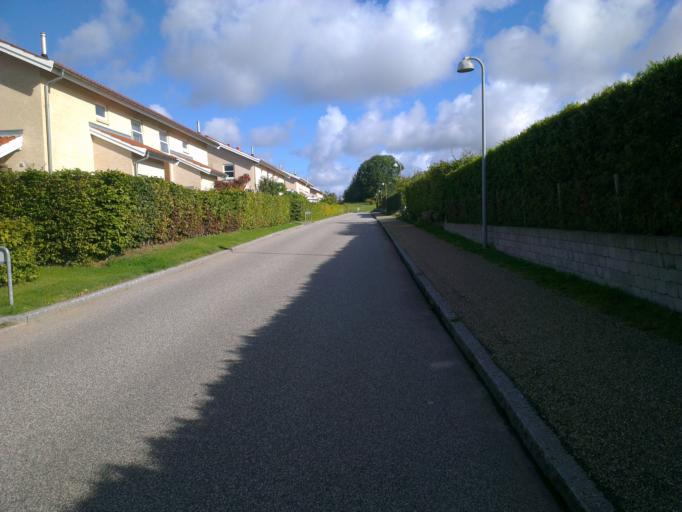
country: DK
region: Capital Region
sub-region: Frederikssund Kommune
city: Slangerup
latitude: 55.8382
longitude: 12.1676
